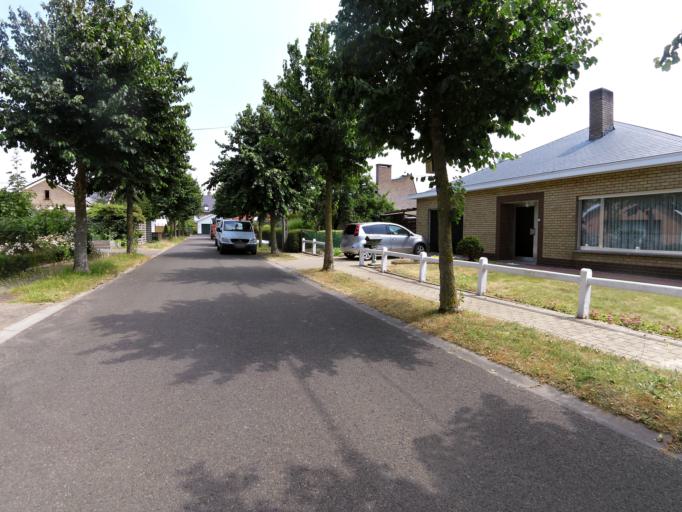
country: BE
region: Flanders
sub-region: Provincie West-Vlaanderen
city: Oudenburg
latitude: 51.1800
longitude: 3.0024
